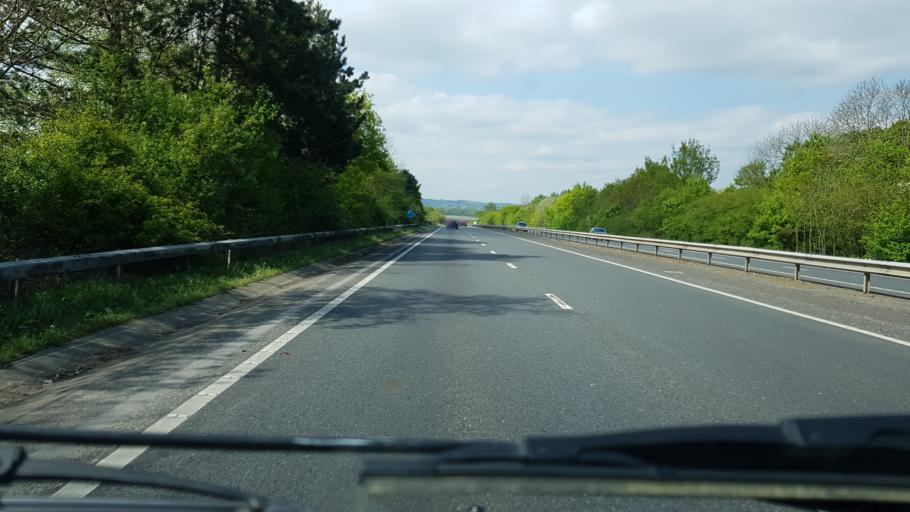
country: GB
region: England
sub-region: Kent
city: Tonbridge
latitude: 51.1942
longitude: 0.2331
